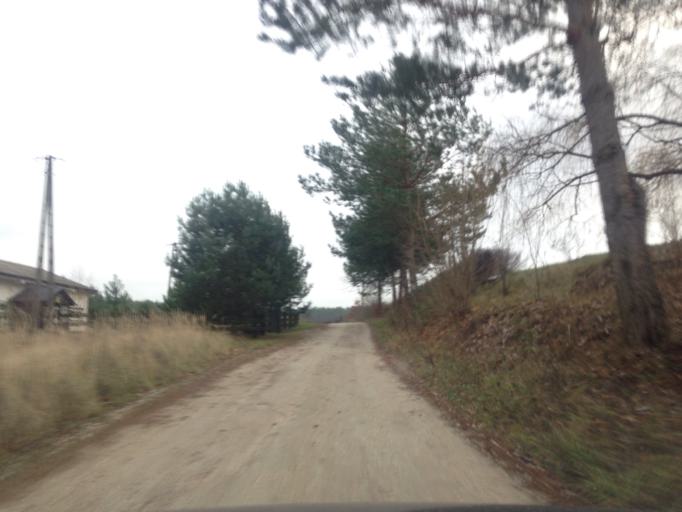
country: PL
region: Kujawsko-Pomorskie
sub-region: Powiat brodnicki
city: Gorzno
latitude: 53.2088
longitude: 19.6717
